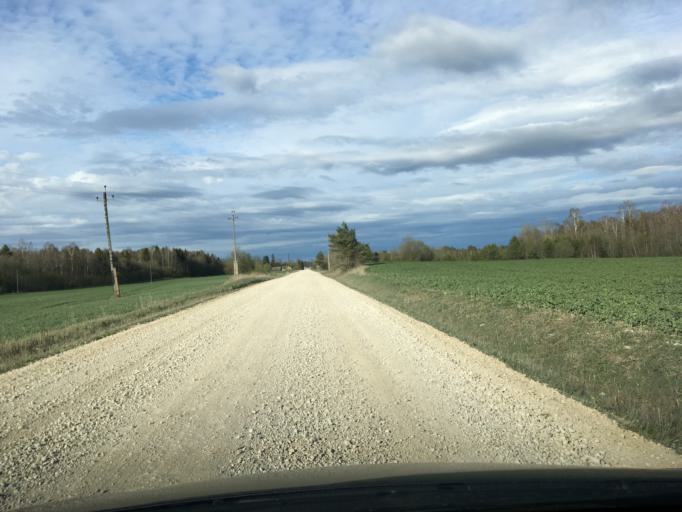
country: EE
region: Raplamaa
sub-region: Maerjamaa vald
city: Marjamaa
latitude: 58.9728
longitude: 24.3451
